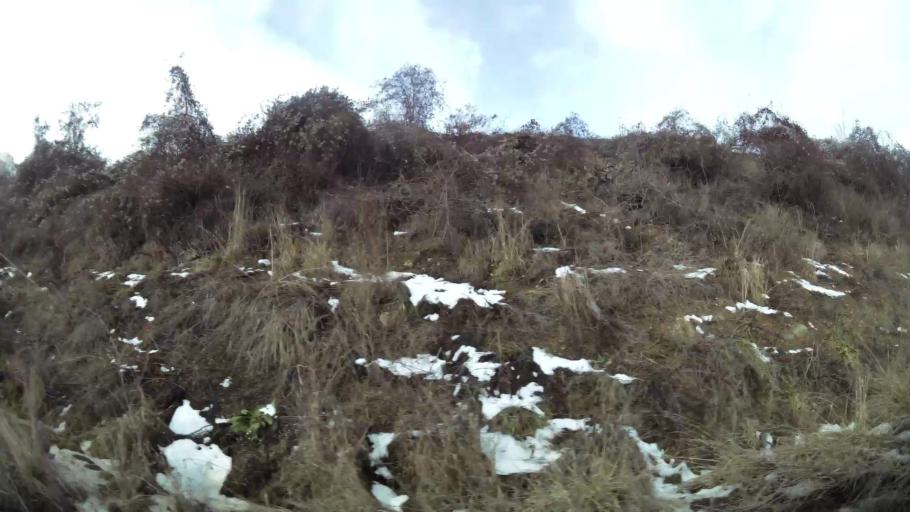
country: XK
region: Pristina
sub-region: Komuna e Prishtines
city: Pristina
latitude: 42.6871
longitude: 21.1769
